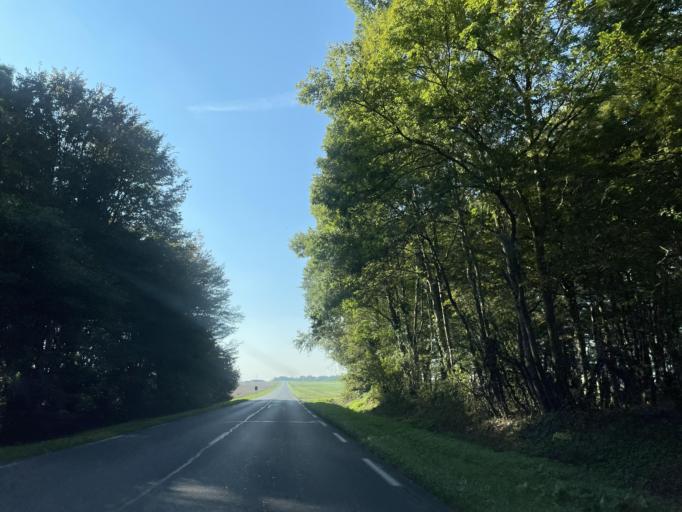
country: FR
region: Ile-de-France
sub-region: Departement de Seine-et-Marne
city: Chailly-en-Brie
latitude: 48.7876
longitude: 3.1477
